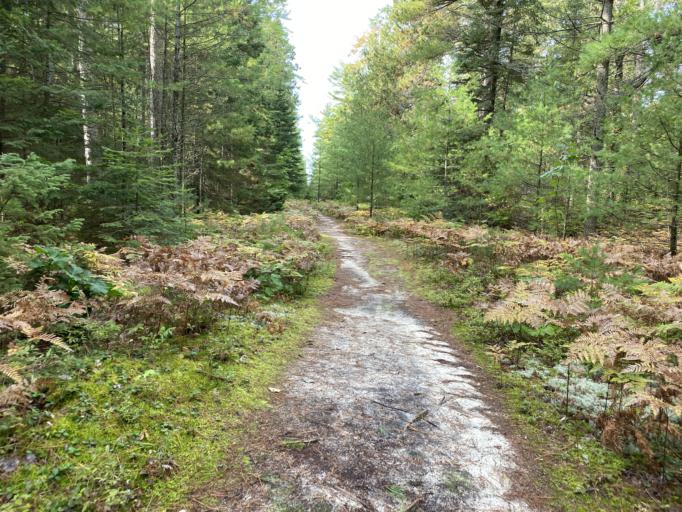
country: US
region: Michigan
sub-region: Mackinac County
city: Saint Ignace
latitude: 45.7505
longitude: -84.8837
